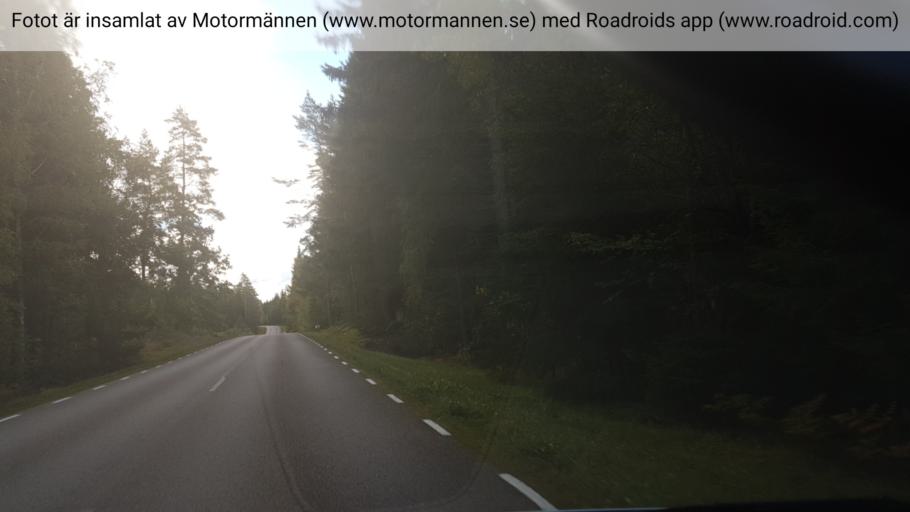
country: SE
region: Vaestra Goetaland
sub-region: Gotene Kommun
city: Goetene
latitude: 58.5448
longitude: 13.6544
